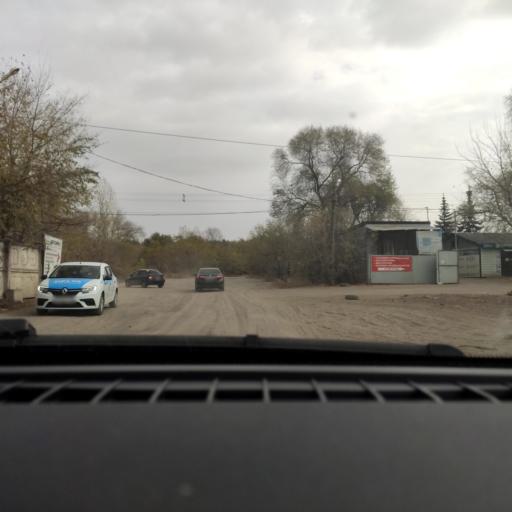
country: RU
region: Voronezj
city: Voronezh
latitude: 51.6853
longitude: 39.2701
